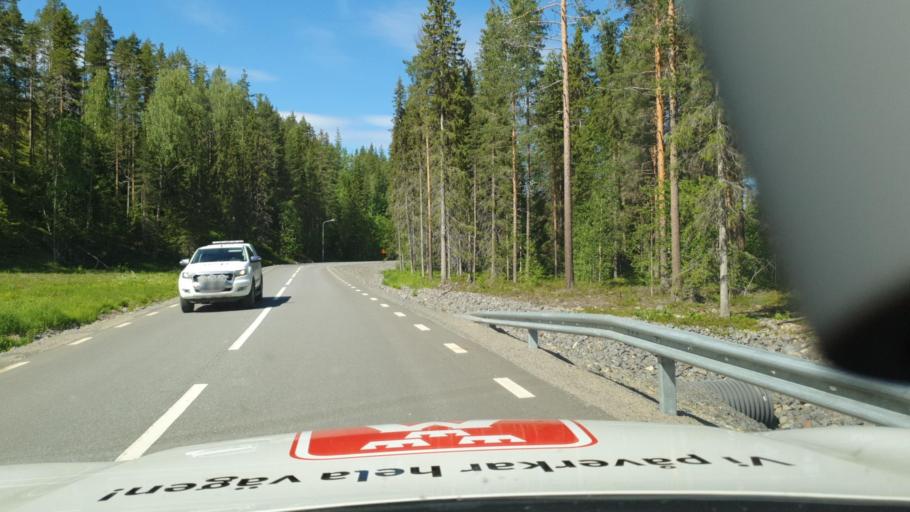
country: SE
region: Vaesterbotten
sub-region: Skelleftea Kommun
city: Boliden
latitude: 64.7889
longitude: 20.3437
